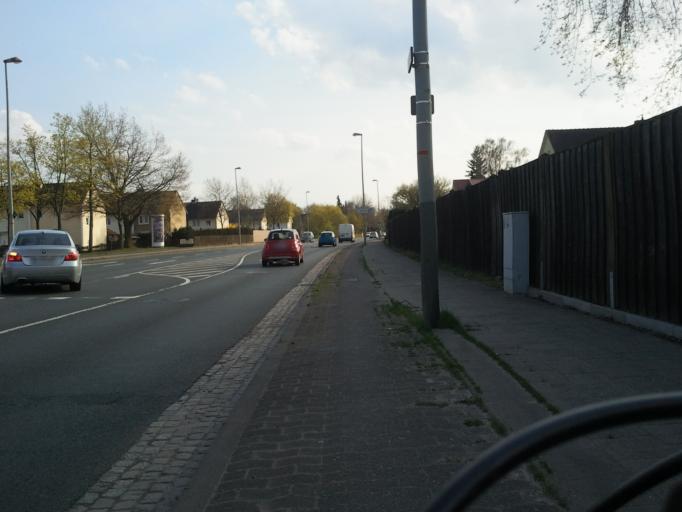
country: DE
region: Lower Saxony
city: Nienburg
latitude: 52.6338
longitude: 9.2198
